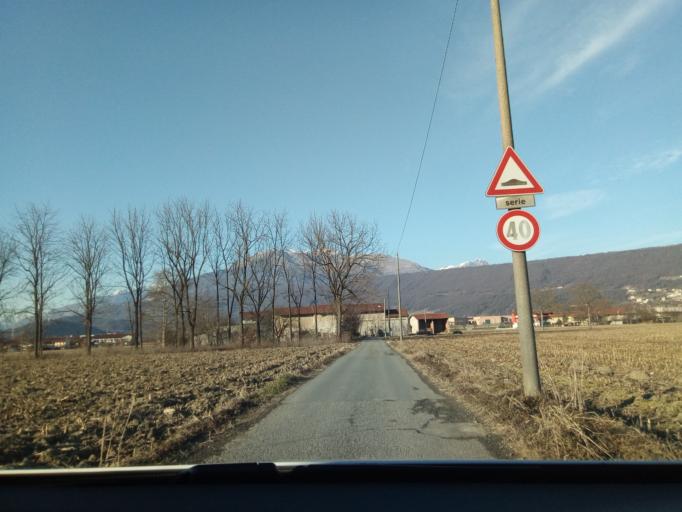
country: IT
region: Piedmont
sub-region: Provincia di Torino
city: Bollengo
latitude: 45.4626
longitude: 7.9210
